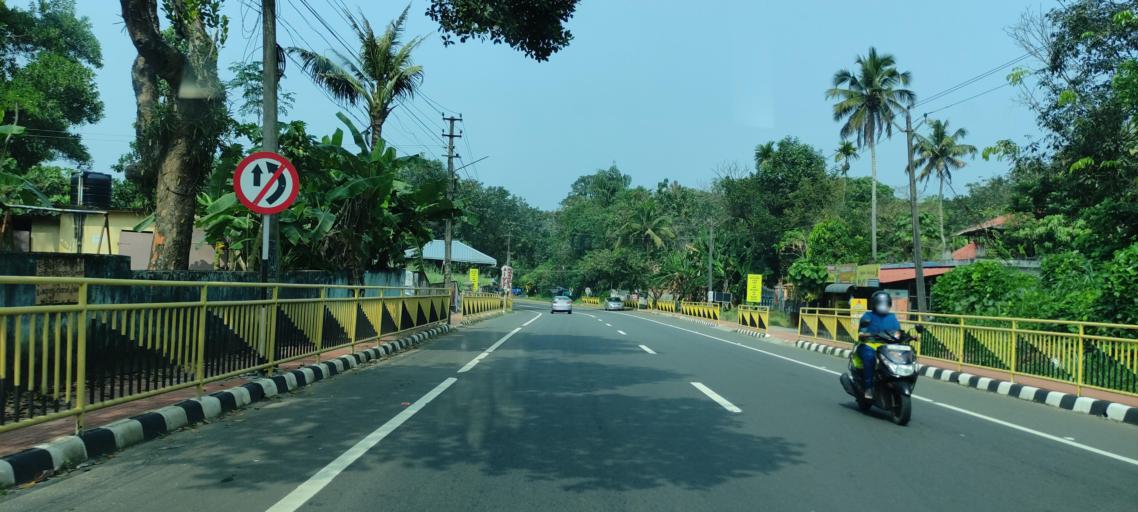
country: IN
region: Kerala
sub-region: Pattanamtitta
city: Adur
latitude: 9.1911
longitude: 76.7054
